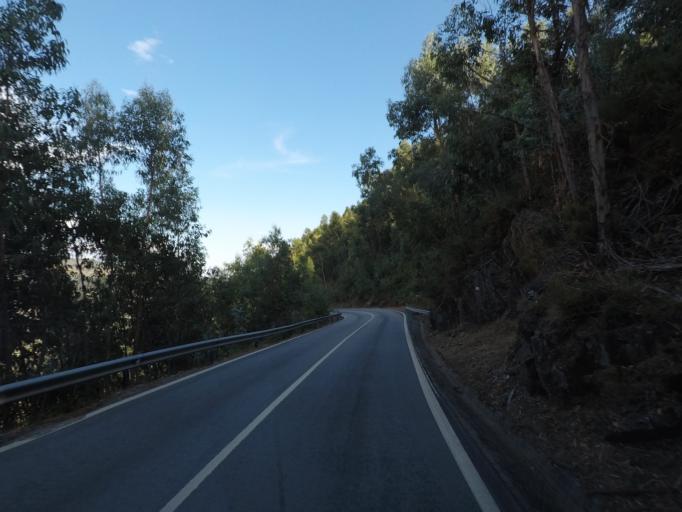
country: PT
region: Vila Real
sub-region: Mesao Frio
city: Mesao Frio
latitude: 41.1760
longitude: -7.9258
